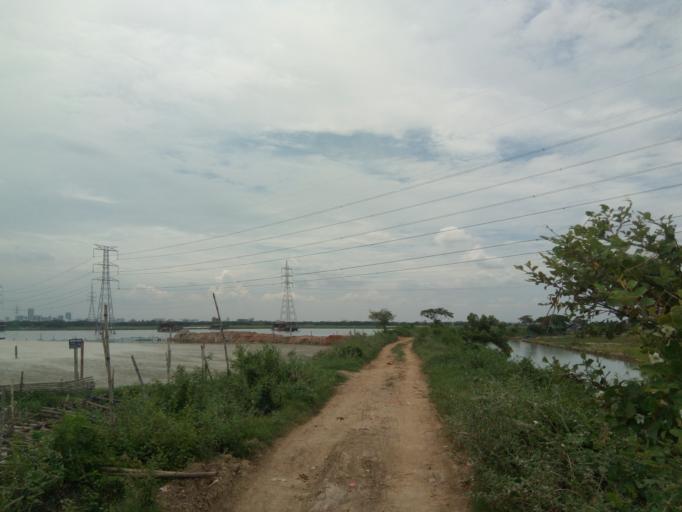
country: BD
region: Dhaka
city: Paltan
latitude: 23.7233
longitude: 90.4622
